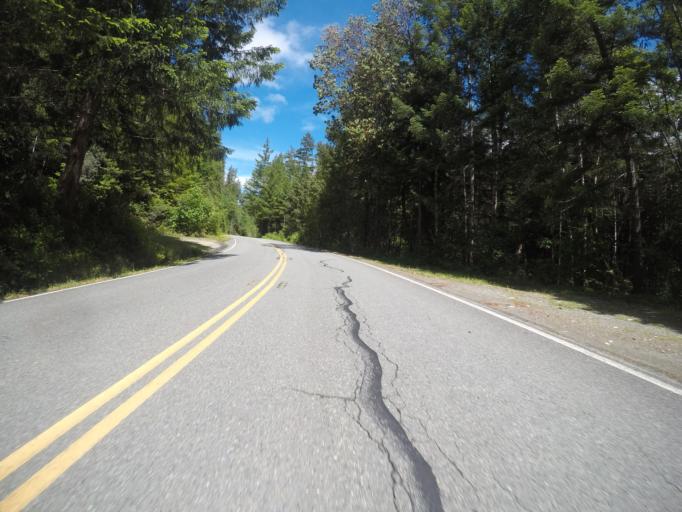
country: US
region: California
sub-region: Del Norte County
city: Bertsch-Oceanview
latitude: 41.7238
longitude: -123.9537
